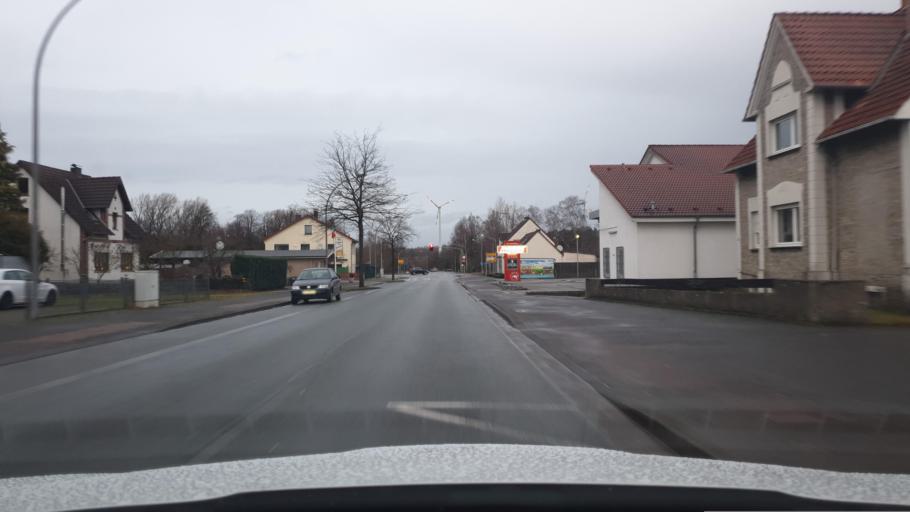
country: DE
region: North Rhine-Westphalia
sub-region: Regierungsbezirk Detmold
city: Lage
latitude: 51.9540
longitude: 8.8125
